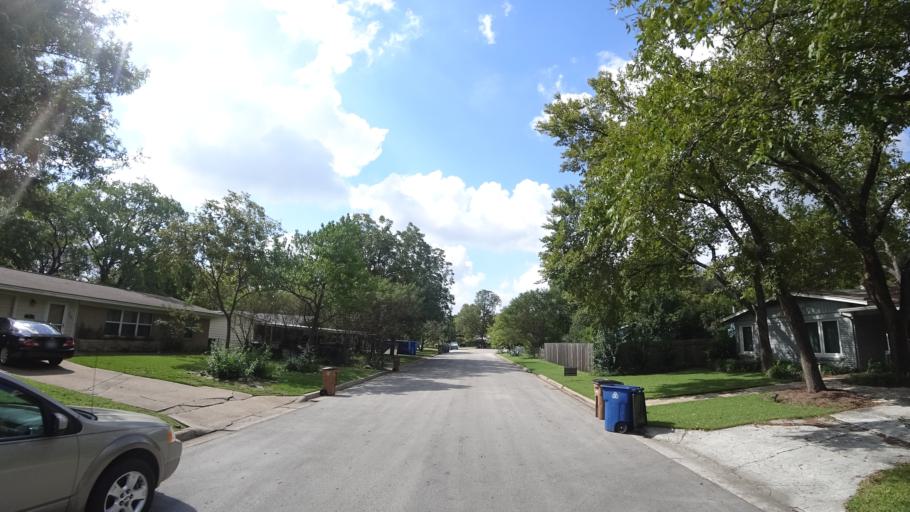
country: US
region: Texas
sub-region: Travis County
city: Austin
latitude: 30.3498
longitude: -97.7211
